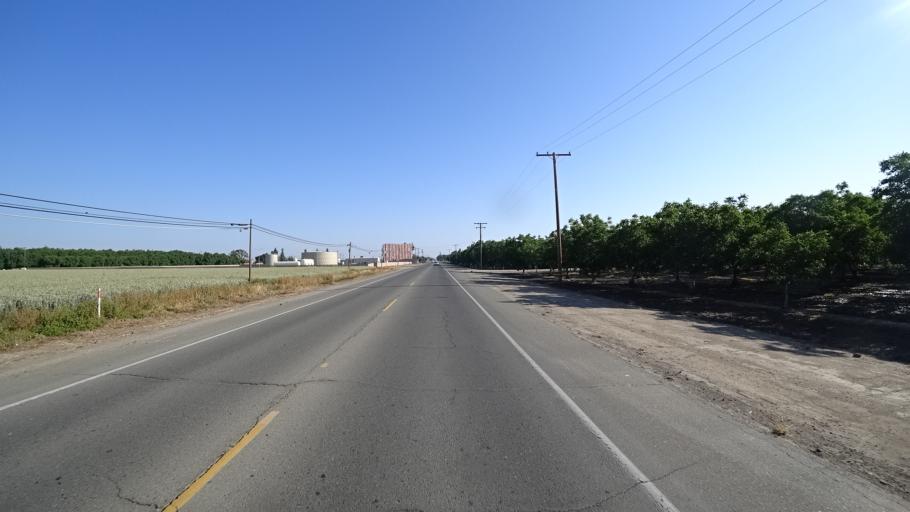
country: US
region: California
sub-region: Kings County
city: Armona
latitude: 36.3237
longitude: -119.7090
